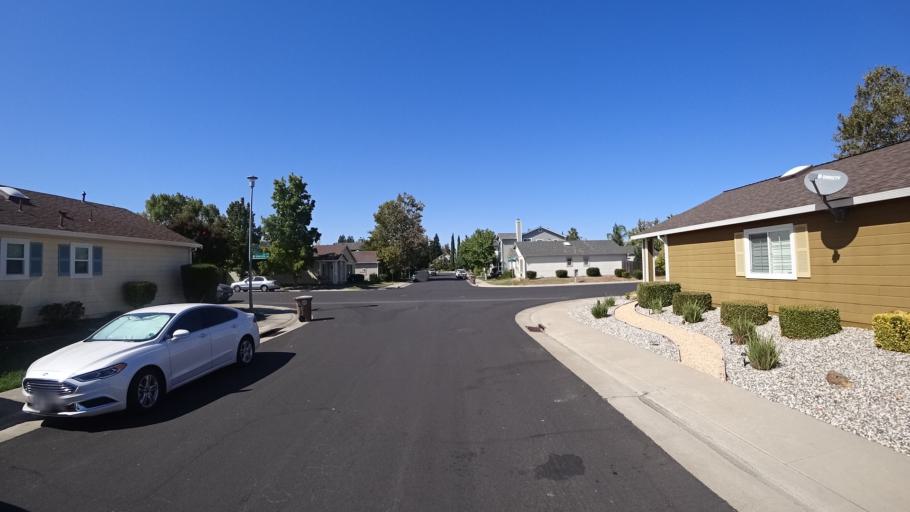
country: US
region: California
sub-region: Sacramento County
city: Laguna
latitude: 38.4325
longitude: -121.4254
